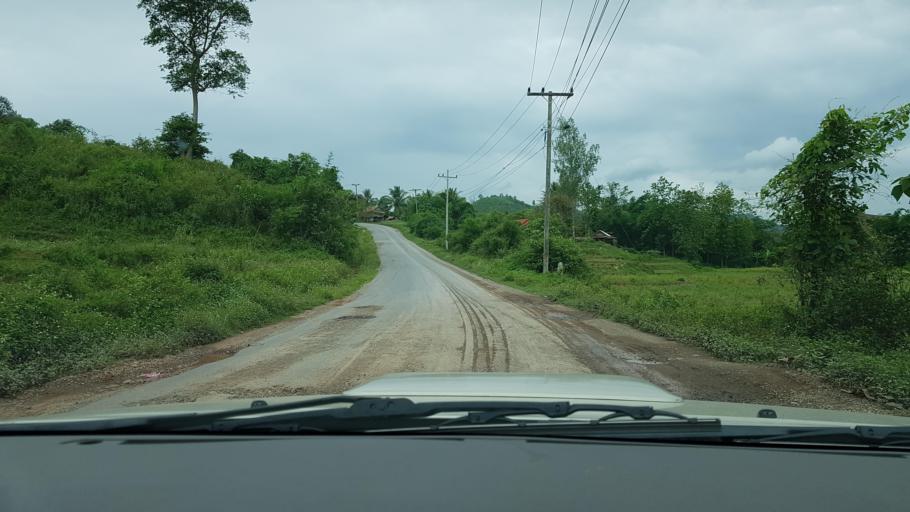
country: LA
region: Loungnamtha
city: Muang Nale
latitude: 20.3683
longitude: 101.7146
